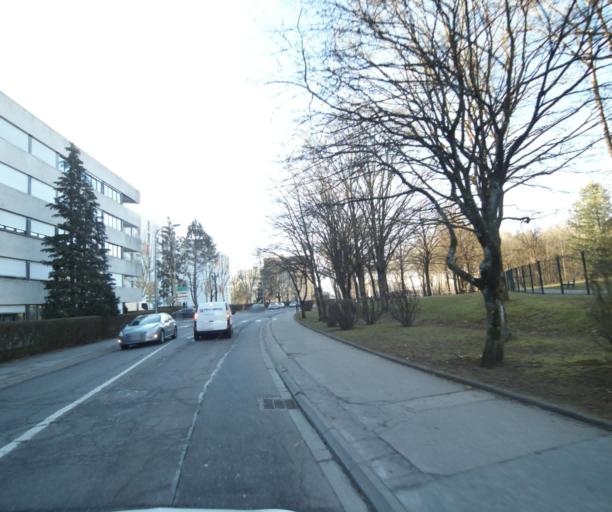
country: FR
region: Lorraine
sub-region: Departement de Meurthe-et-Moselle
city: Laxou
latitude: 48.6990
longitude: 6.1321
